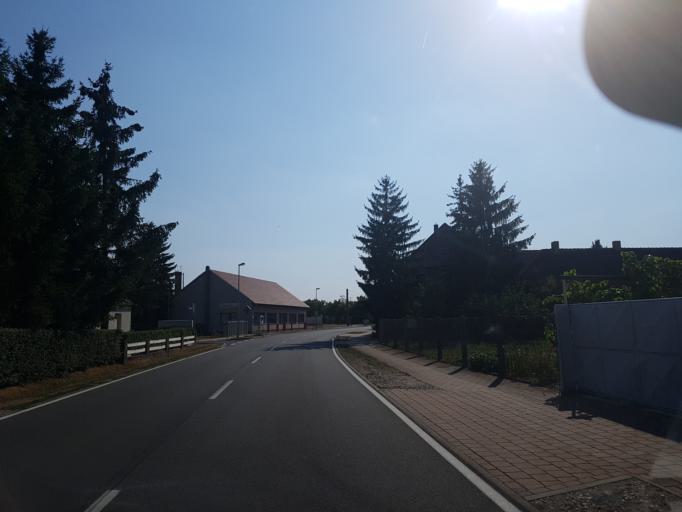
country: DE
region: Saxony-Anhalt
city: Annaburg
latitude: 51.6964
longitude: 13.0065
